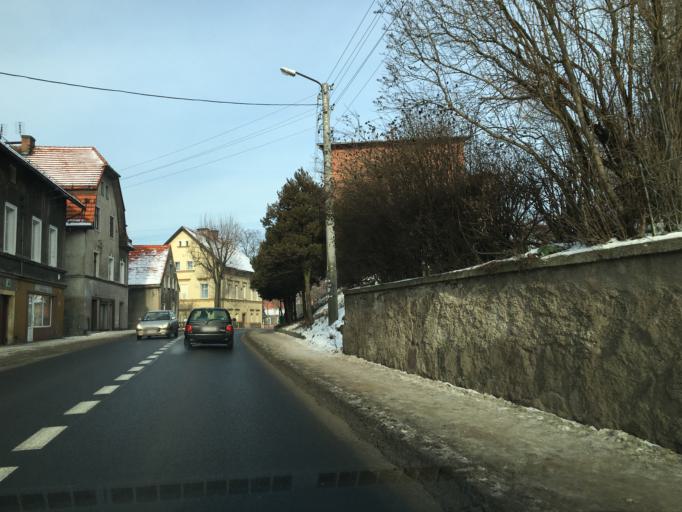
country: PL
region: Lower Silesian Voivodeship
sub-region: Powiat walbrzyski
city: Gluszyca
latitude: 50.6796
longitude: 16.3790
